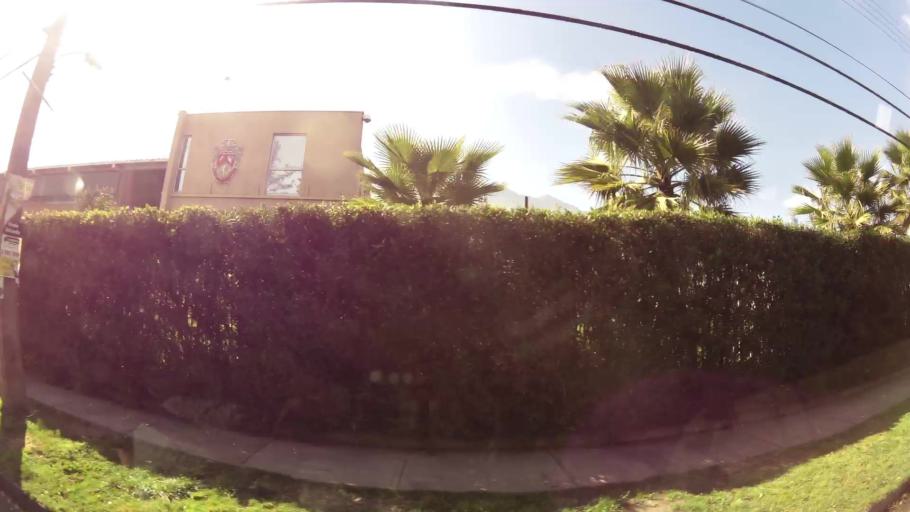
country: CL
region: Santiago Metropolitan
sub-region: Provincia de Santiago
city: Villa Presidente Frei, Nunoa, Santiago, Chile
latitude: -33.4514
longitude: -70.5281
